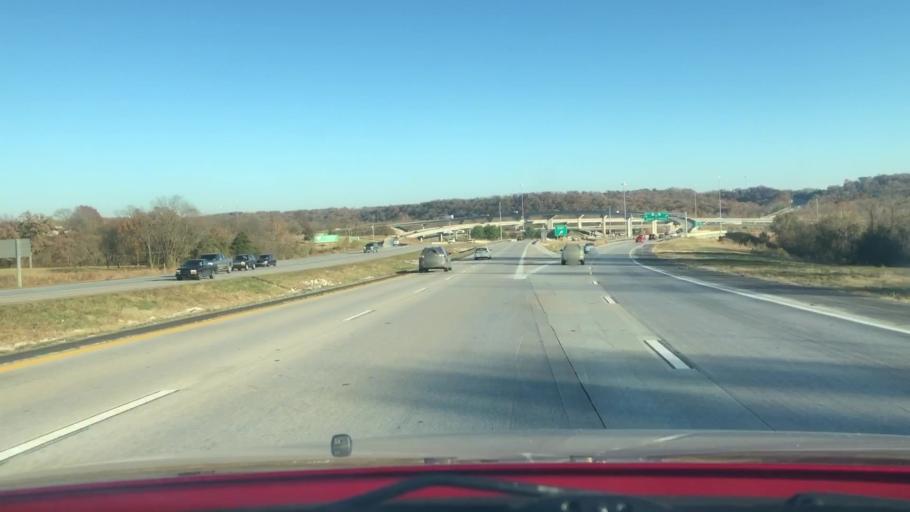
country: US
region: Missouri
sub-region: Christian County
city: Nixa
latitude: 37.1304
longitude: -93.2385
